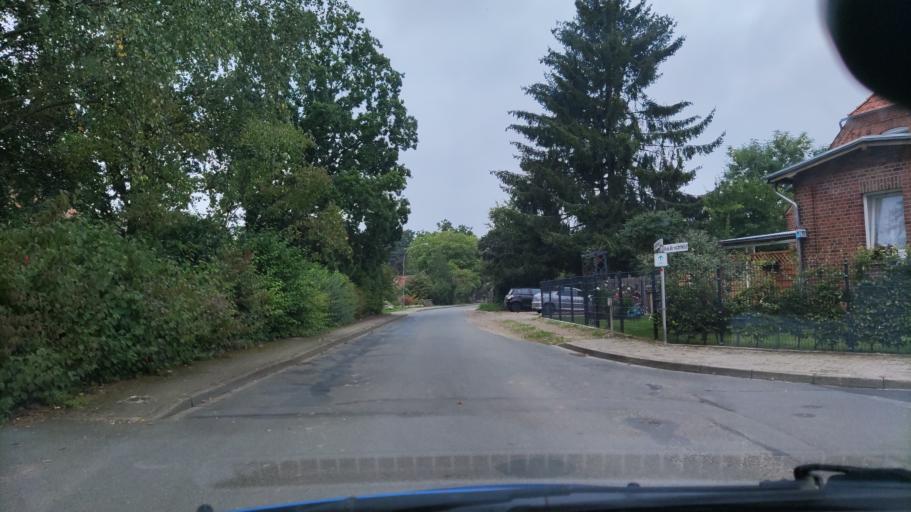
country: DE
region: Lower Saxony
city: Altenmedingen
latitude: 53.1304
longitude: 10.6065
